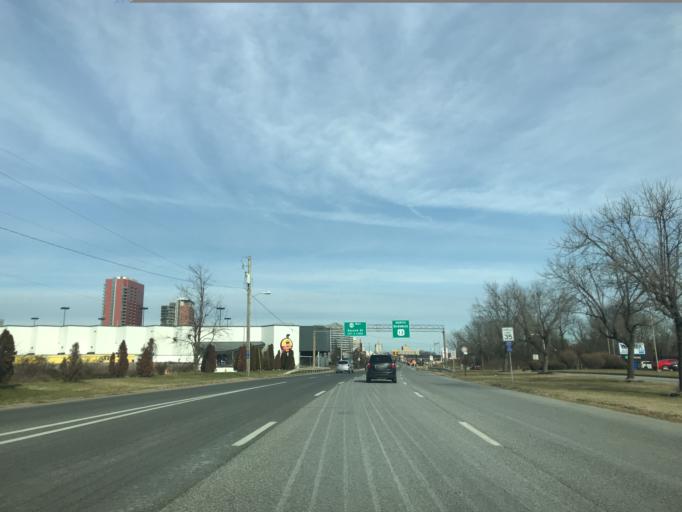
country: US
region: Delaware
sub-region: New Castle County
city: Wilmington
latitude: 39.7298
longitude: -75.5549
